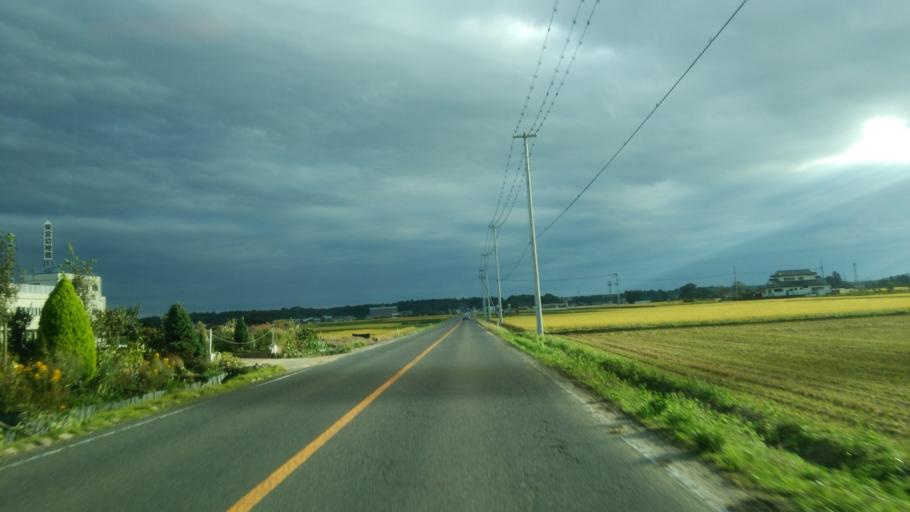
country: JP
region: Fukushima
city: Koriyama
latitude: 37.3735
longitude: 140.3410
